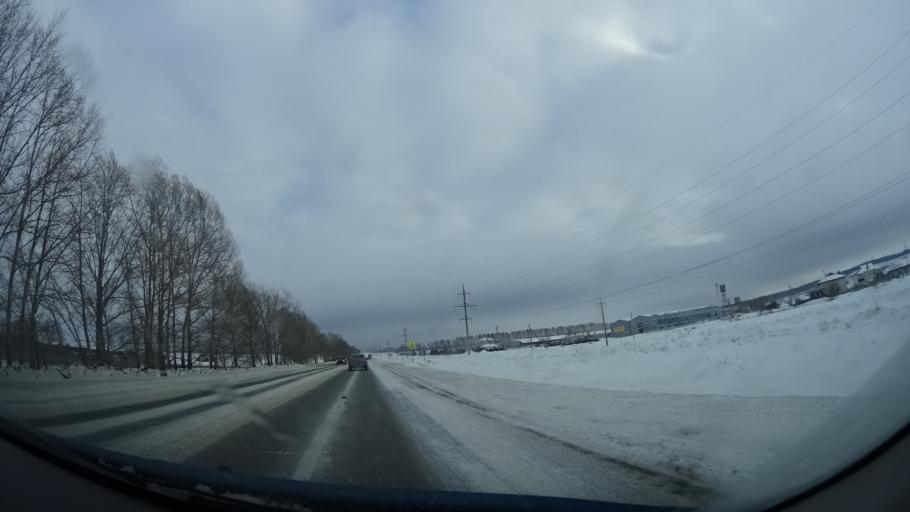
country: RU
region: Bashkortostan
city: Mikhaylovka
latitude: 54.8656
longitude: 55.7475
